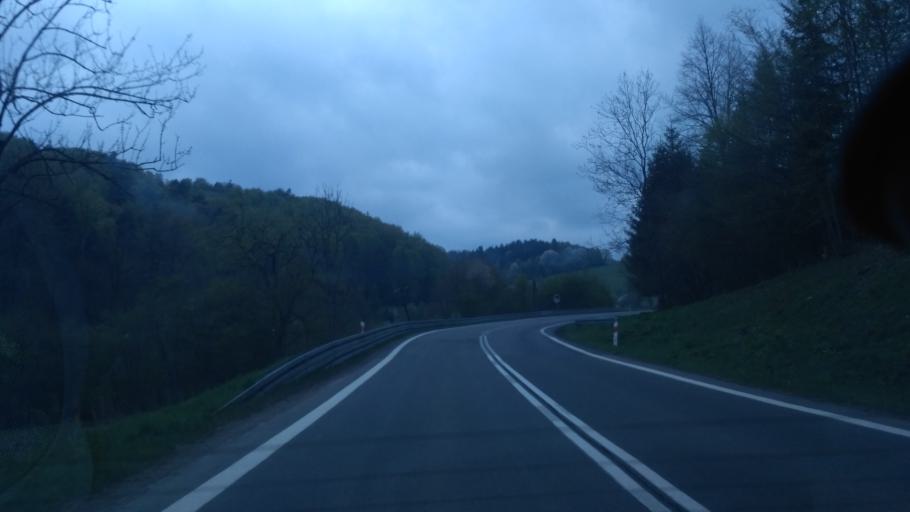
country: PL
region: Subcarpathian Voivodeship
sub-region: Powiat sanocki
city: Zagorz
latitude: 49.5405
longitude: 22.3025
